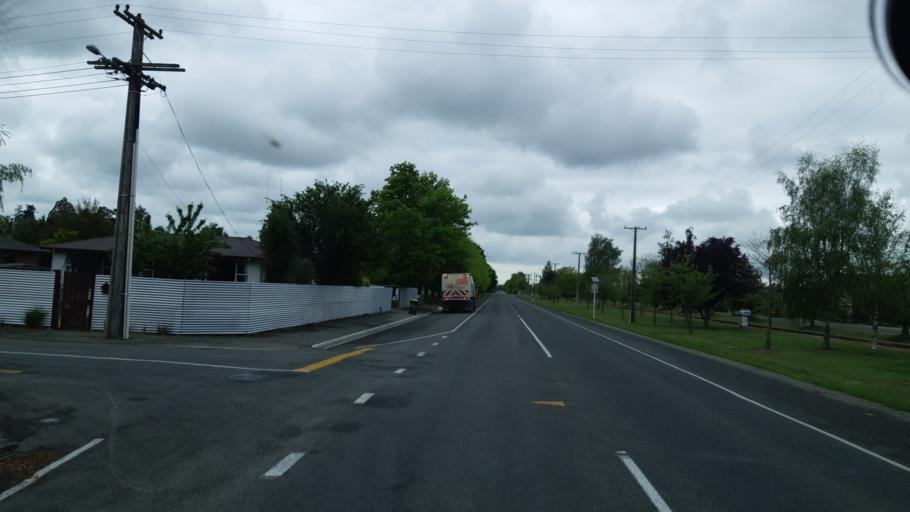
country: NZ
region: Canterbury
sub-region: Timaru District
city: Pleasant Point
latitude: -44.2632
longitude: 171.1383
